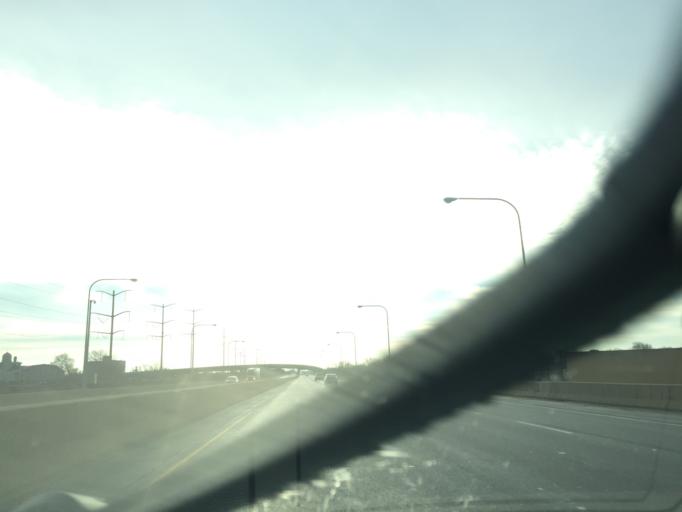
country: US
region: Illinois
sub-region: Cook County
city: Chicago
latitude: 41.7534
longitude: -87.5909
